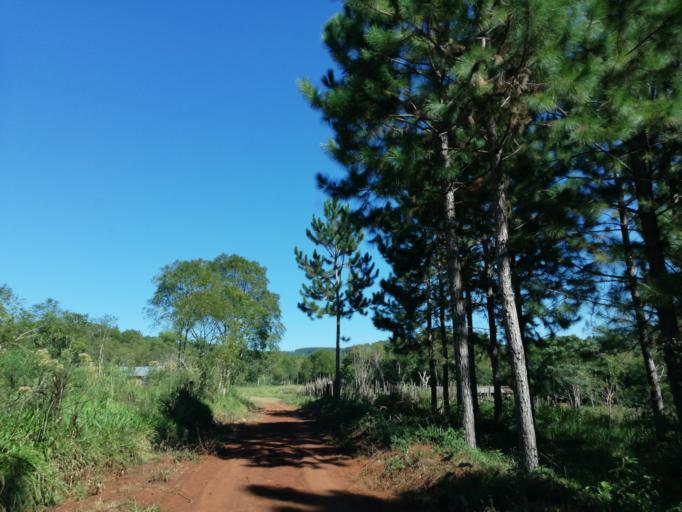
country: AR
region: Misiones
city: El Soberbio
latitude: -27.0640
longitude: -54.3783
